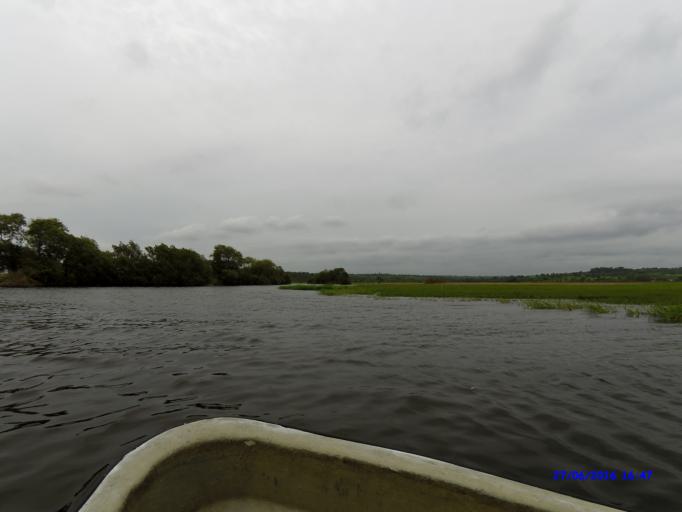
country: BJ
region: Atlantique
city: Allada
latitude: 6.6016
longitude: 1.9939
